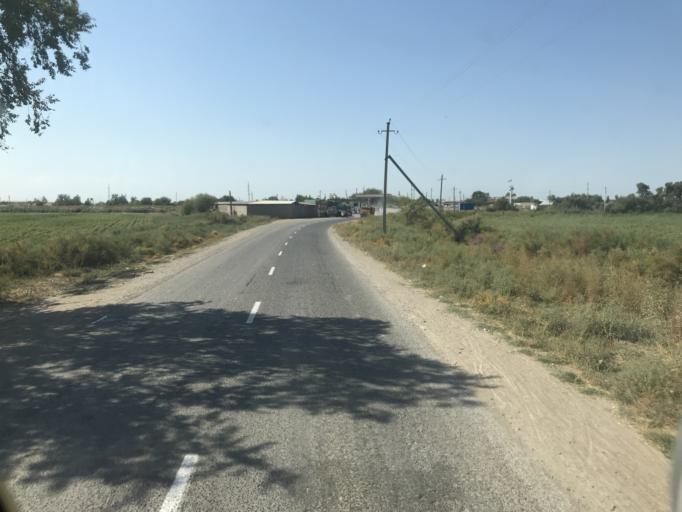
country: KZ
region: Ongtustik Qazaqstan
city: Myrzakent
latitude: 40.6717
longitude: 68.5528
